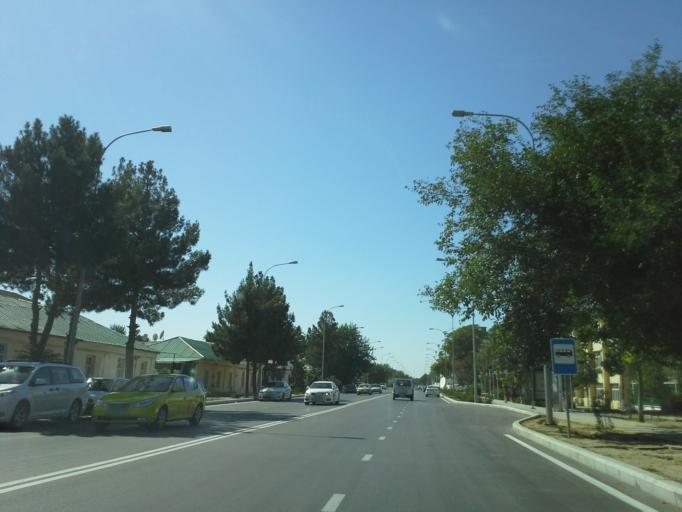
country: TM
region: Ahal
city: Ashgabat
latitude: 37.9521
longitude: 58.3882
